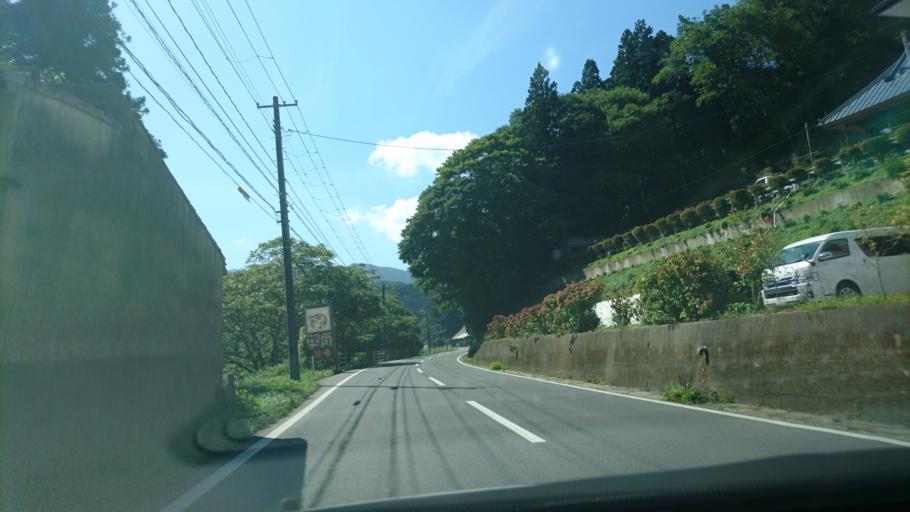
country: JP
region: Iwate
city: Ofunato
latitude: 39.0211
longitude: 141.5526
